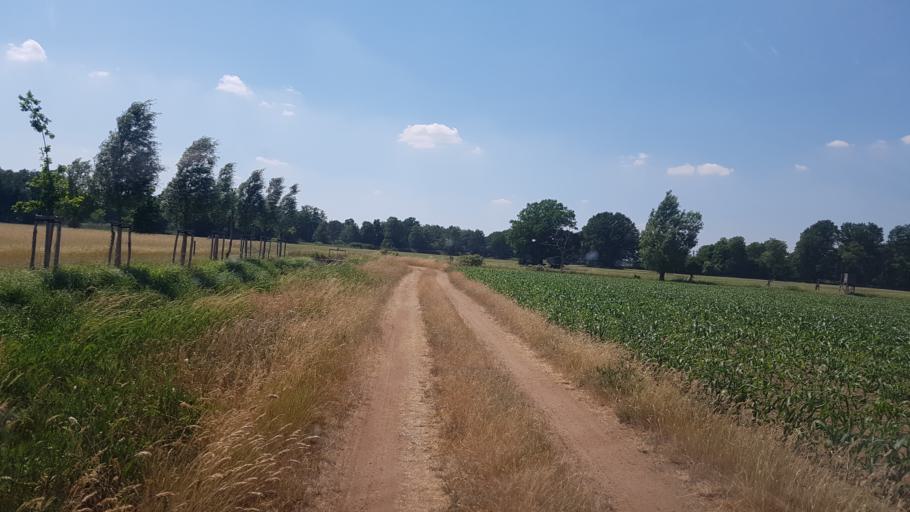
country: DE
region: Brandenburg
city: Herzberg
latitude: 51.6722
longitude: 13.2641
